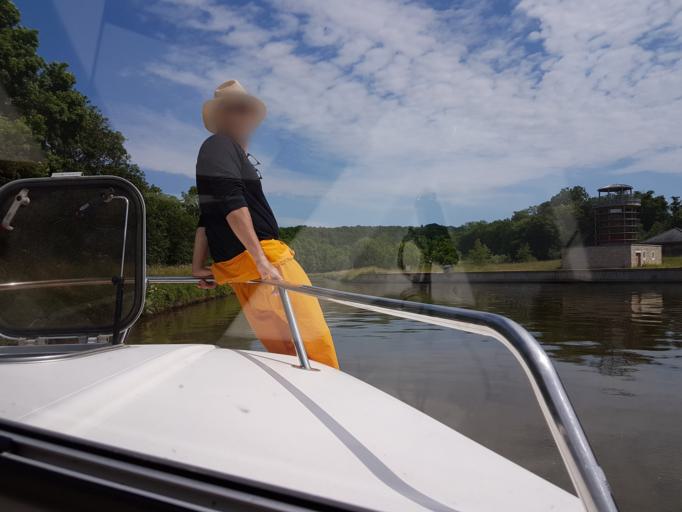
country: FR
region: Bourgogne
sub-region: Departement de la Nievre
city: Clamecy
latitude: 47.4540
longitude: 3.5389
